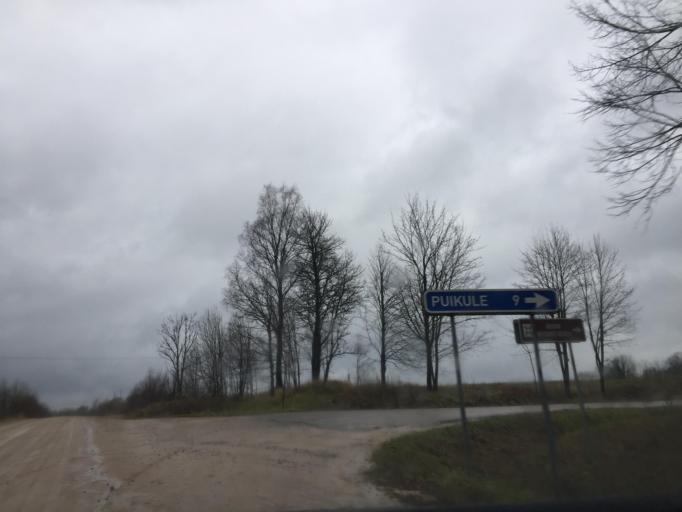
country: LV
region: Aloja
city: Aloja
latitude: 57.6600
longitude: 24.7742
